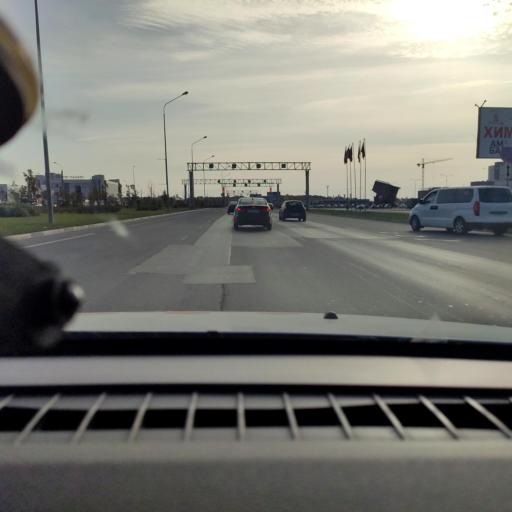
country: RU
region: Samara
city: Samara
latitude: 53.1411
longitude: 50.1777
